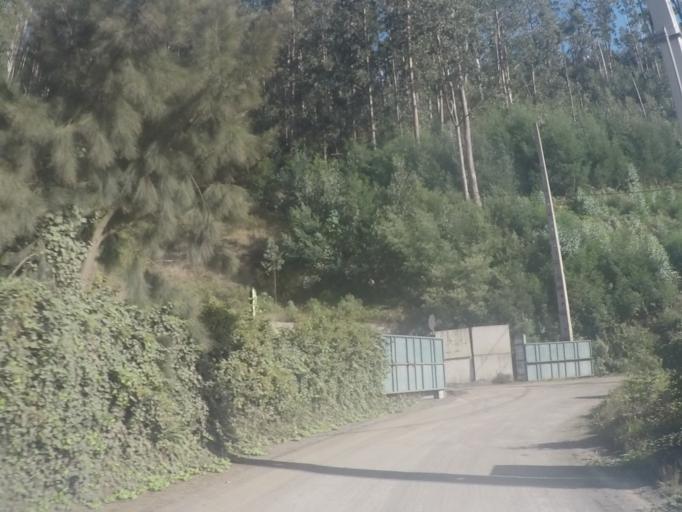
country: PT
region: Madeira
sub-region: Funchal
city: Nossa Senhora do Monte
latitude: 32.6925
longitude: -16.9074
